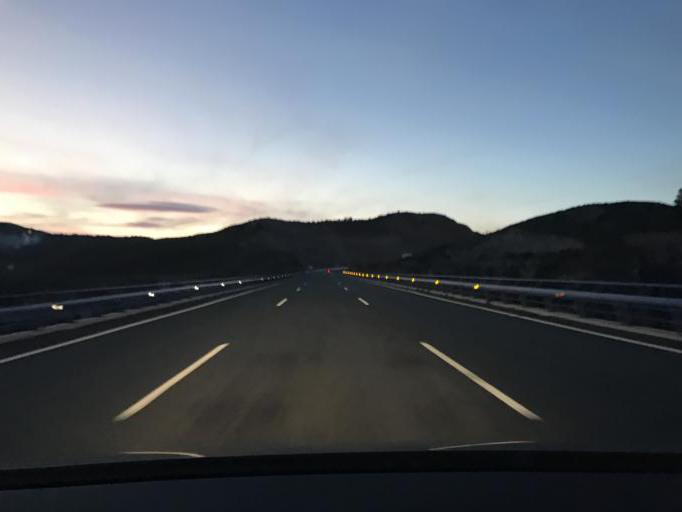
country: ES
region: Andalusia
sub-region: Provincia de Granada
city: Lanjaron
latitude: 36.9137
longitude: -3.5292
